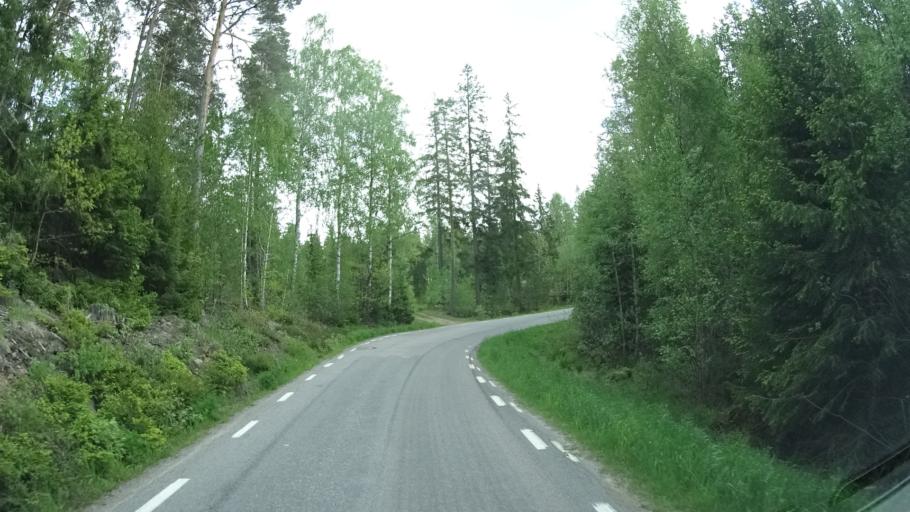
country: SE
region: OEstergoetland
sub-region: Finspangs Kommun
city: Finspang
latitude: 58.5998
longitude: 15.7640
